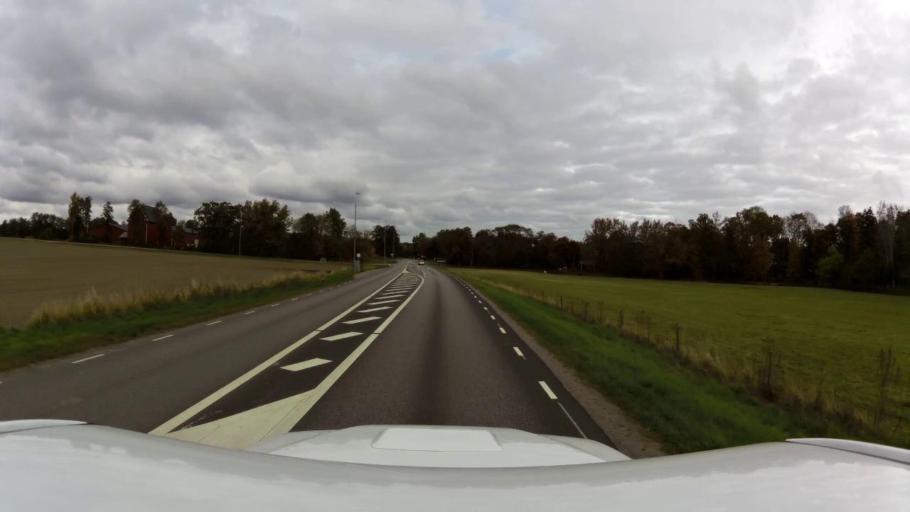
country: SE
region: OEstergoetland
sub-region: Linkopings Kommun
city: Berg
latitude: 58.4991
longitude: 15.5357
